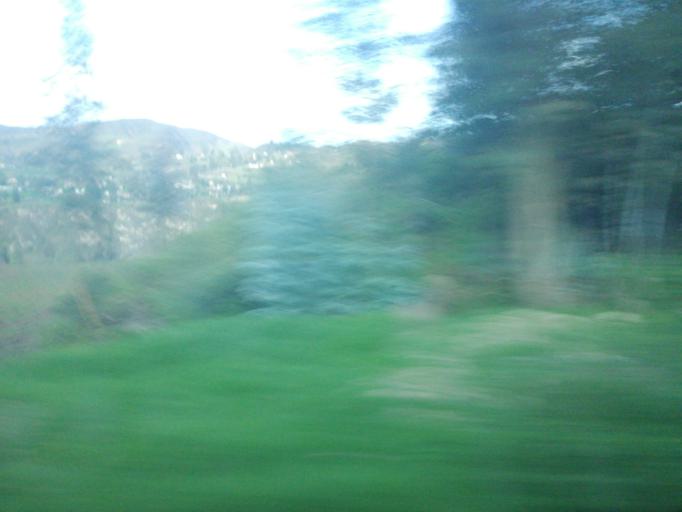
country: EC
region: Azuay
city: Nulti
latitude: -3.0321
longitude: -78.8022
